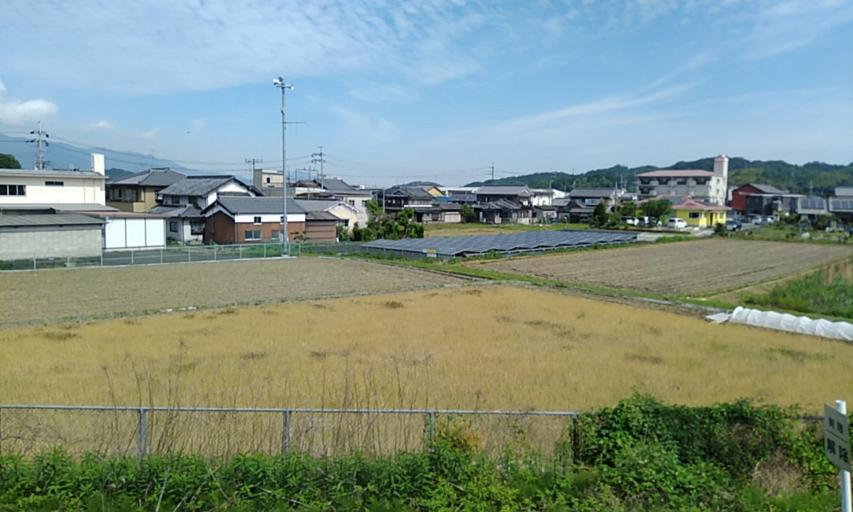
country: JP
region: Nara
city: Gose
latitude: 34.4421
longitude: 135.7771
